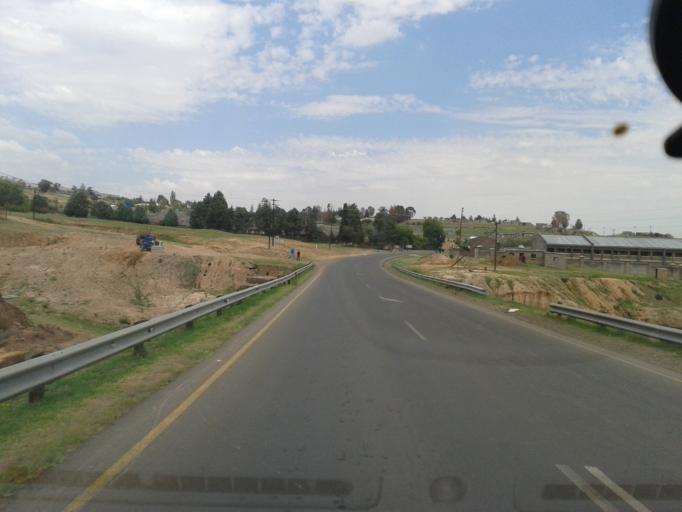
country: LS
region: Maseru
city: Maseru
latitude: -29.3481
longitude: 27.6624
